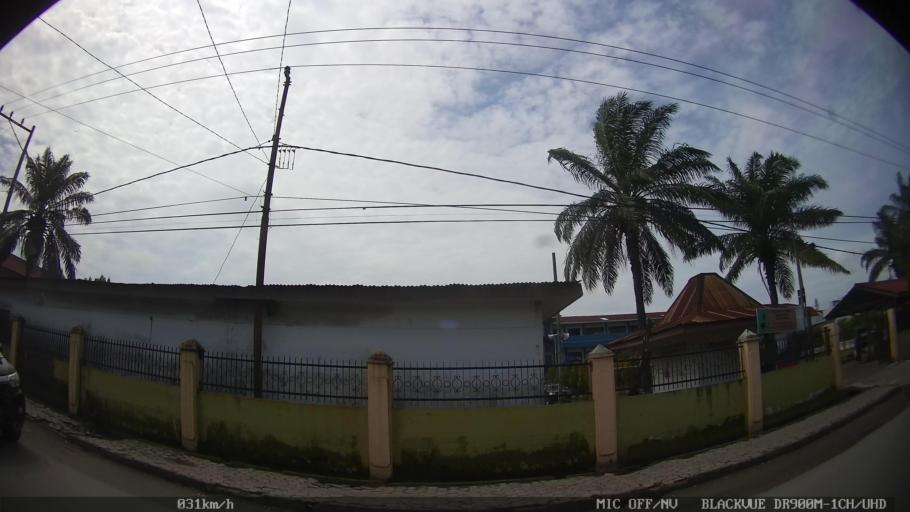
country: ID
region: North Sumatra
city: Medan
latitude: 3.5869
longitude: 98.7254
